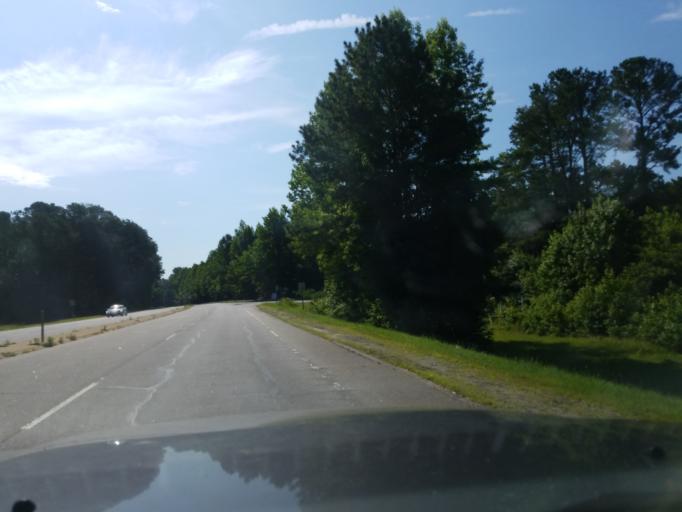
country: US
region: North Carolina
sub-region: Granville County
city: Oxford
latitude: 36.3143
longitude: -78.5416
